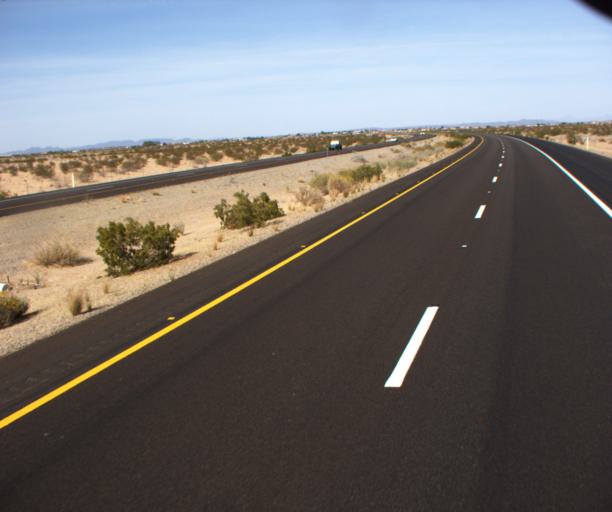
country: US
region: Arizona
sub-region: Yuma County
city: Fortuna Foothills
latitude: 32.6131
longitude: -114.5238
